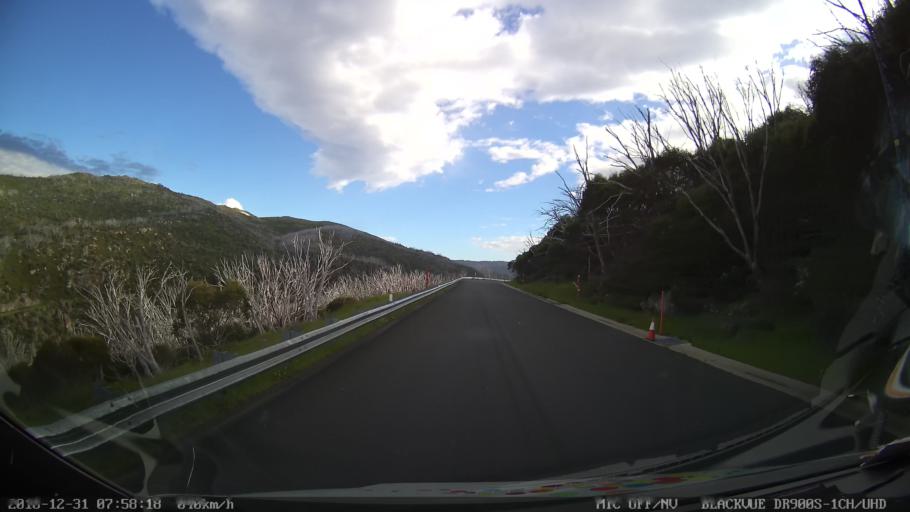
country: AU
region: New South Wales
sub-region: Snowy River
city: Jindabyne
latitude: -36.3754
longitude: 148.3789
